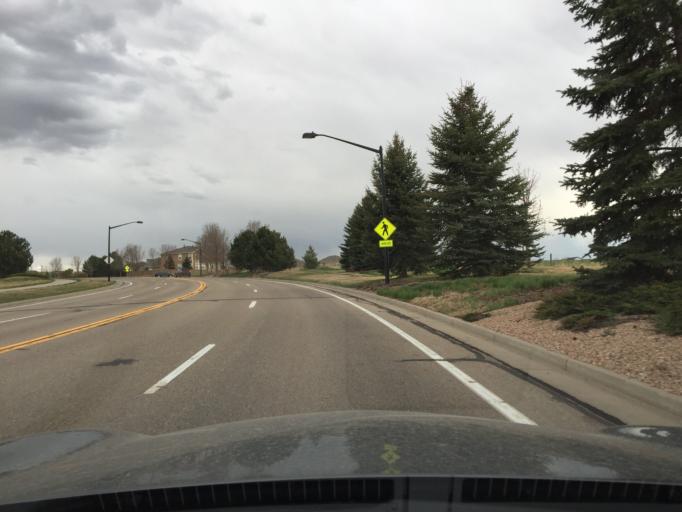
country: US
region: Colorado
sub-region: Boulder County
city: Erie
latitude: 40.0069
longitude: -105.0310
